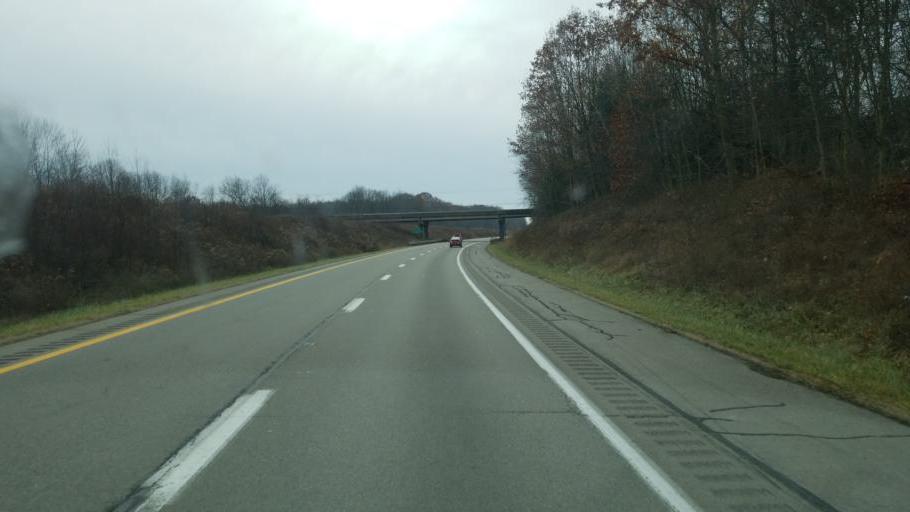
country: US
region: Pennsylvania
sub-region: Crawford County
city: Meadville
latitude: 41.5226
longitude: -80.1695
